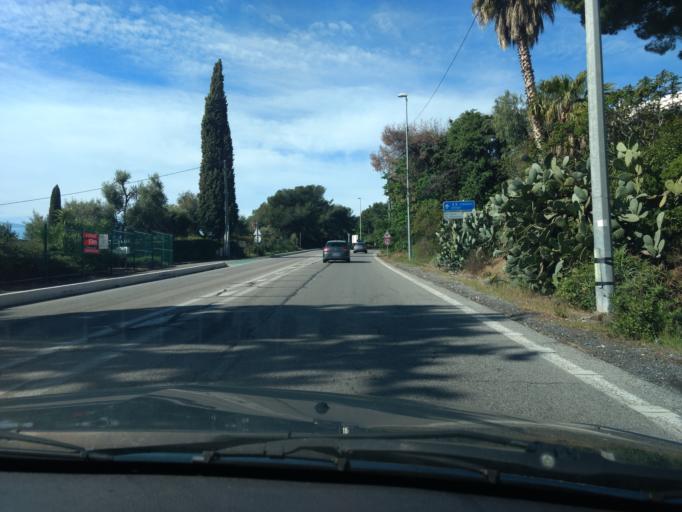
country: FR
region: Provence-Alpes-Cote d'Azur
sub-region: Departement des Alpes-Maritimes
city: Biot
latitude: 43.6348
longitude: 7.1280
